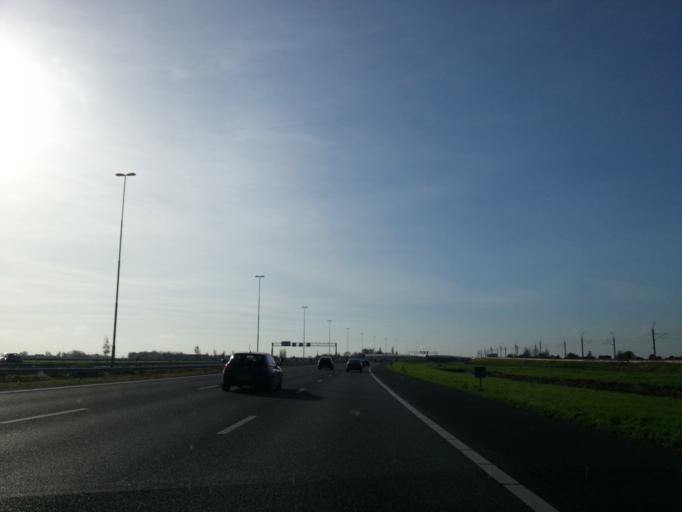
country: NL
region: South Holland
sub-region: Gemeente Kaag en Braassem
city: Oude Wetering
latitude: 52.1866
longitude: 4.6014
